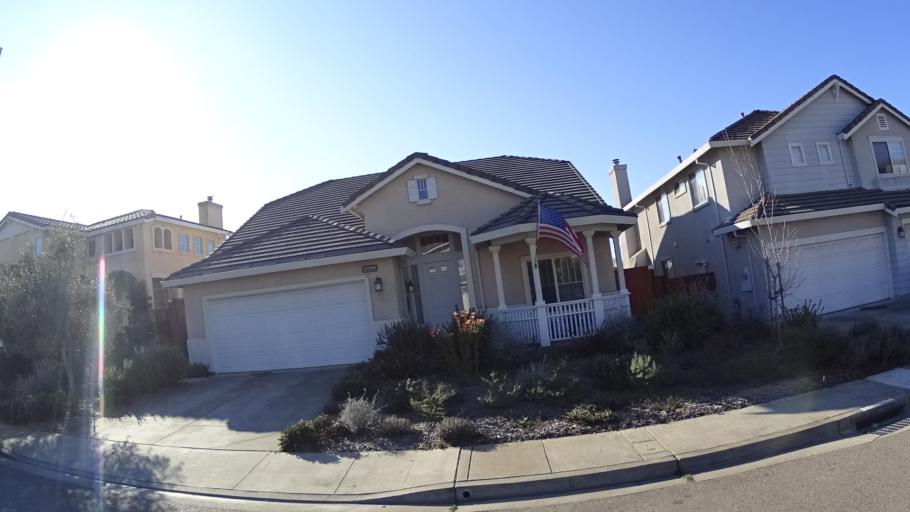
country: US
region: California
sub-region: Alameda County
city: Fairview
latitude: 37.6900
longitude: -122.0360
